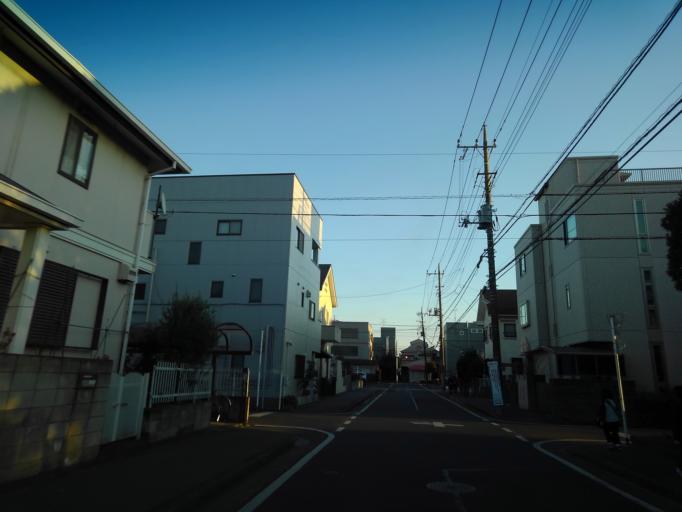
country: JP
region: Saitama
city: Tokorozawa
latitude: 35.7995
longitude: 139.5150
